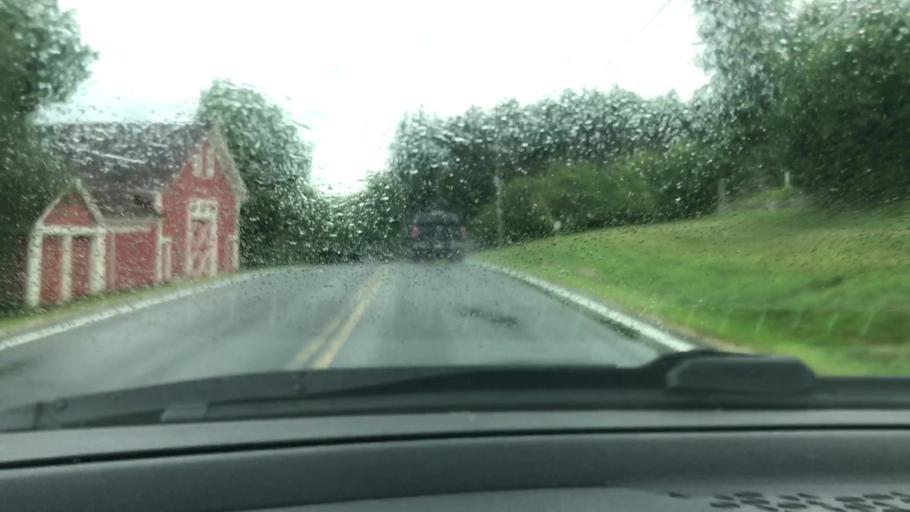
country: US
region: New Hampshire
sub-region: Merrimack County
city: Epsom
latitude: 43.1900
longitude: -71.2689
